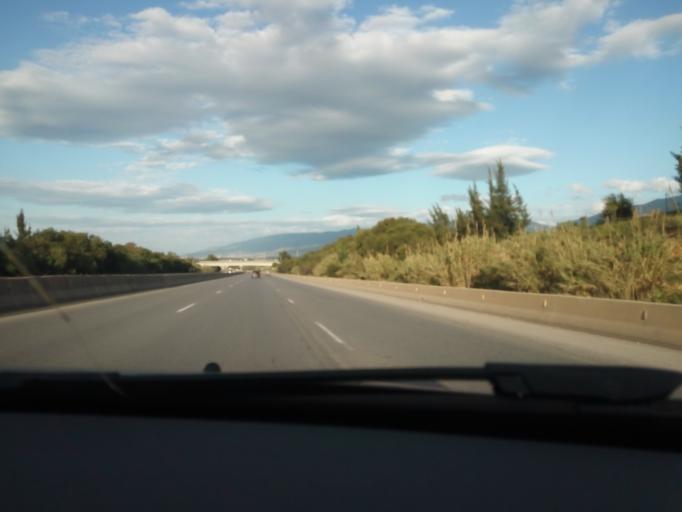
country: DZ
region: Tipaza
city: El Affroun
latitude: 36.4460
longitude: 2.6353
